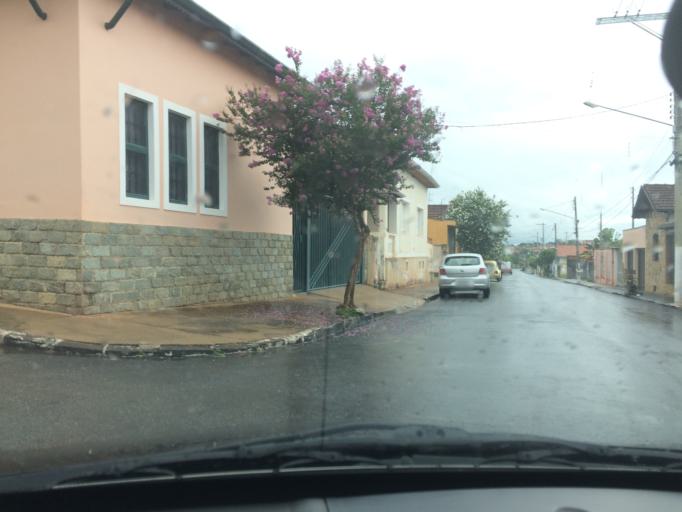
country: BR
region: Sao Paulo
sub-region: Casa Branca
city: Casa Branca
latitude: -21.7701
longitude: -47.0870
